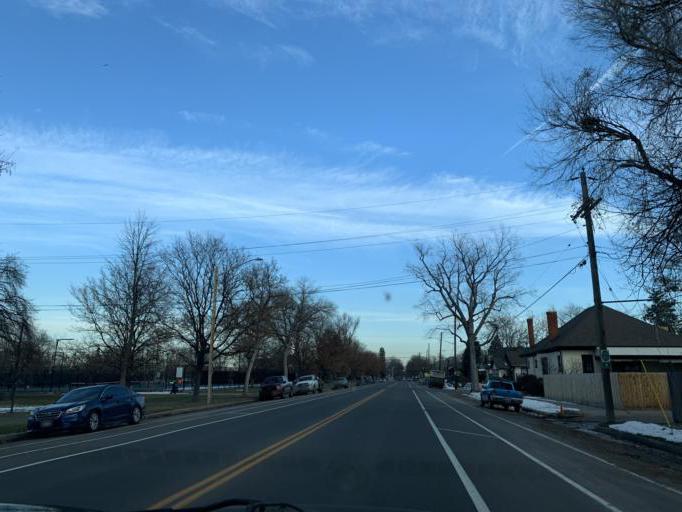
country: US
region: Colorado
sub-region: Jefferson County
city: Edgewater
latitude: 39.7802
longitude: -105.0472
